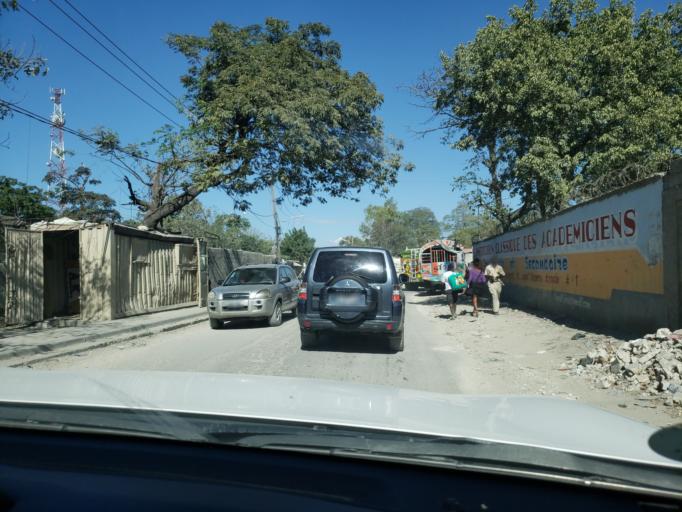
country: HT
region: Ouest
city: Croix des Bouquets
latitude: 18.5747
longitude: -72.2284
